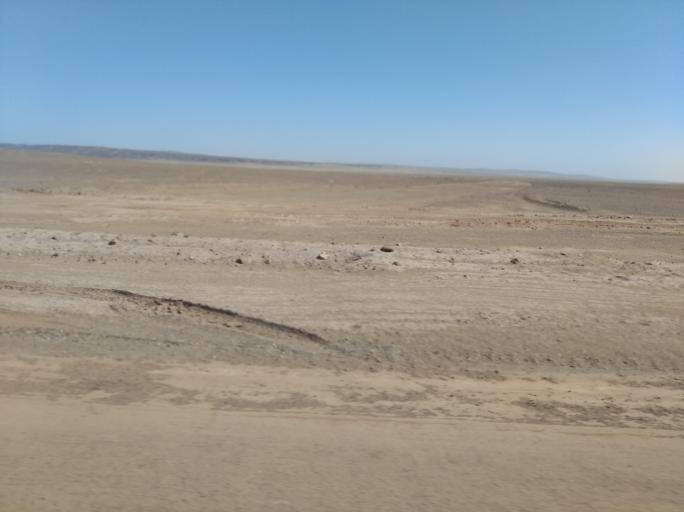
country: CL
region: Atacama
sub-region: Provincia de Copiapo
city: Copiapo
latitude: -27.3237
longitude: -70.8094
